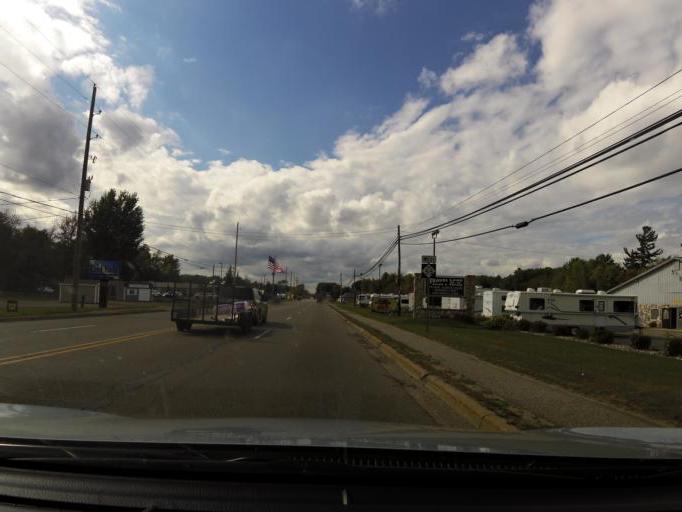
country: US
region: Michigan
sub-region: Roscommon County
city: Prudenville
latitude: 44.2987
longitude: -84.6877
